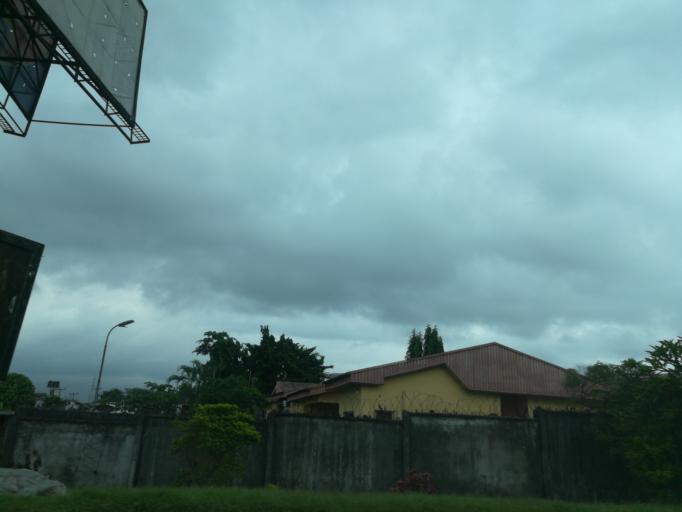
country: NG
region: Rivers
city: Port Harcourt
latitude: 4.8405
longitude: 7.0312
